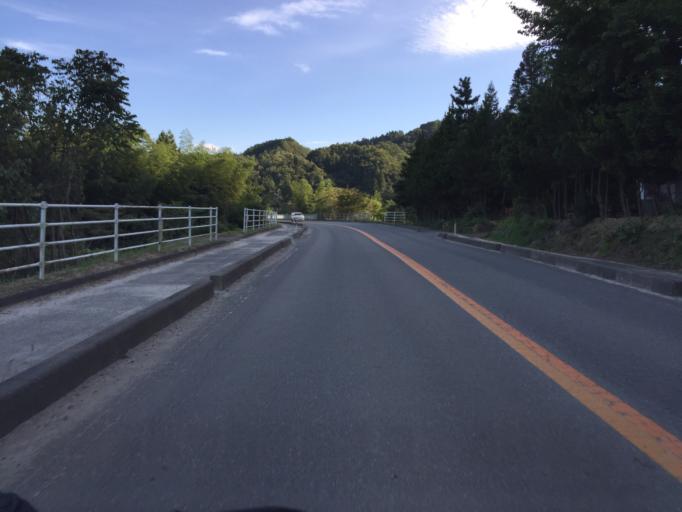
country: JP
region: Fukushima
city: Hobaramachi
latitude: 37.6933
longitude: 140.6089
